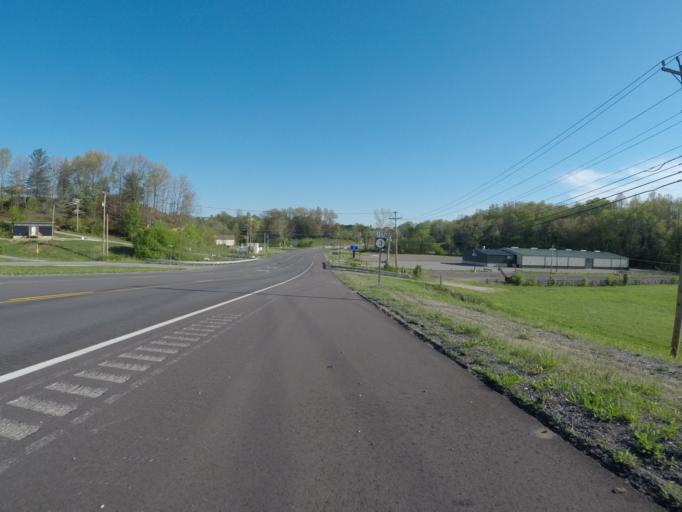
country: US
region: Kentucky
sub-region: Boyd County
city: Meads
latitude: 38.3590
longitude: -82.6976
